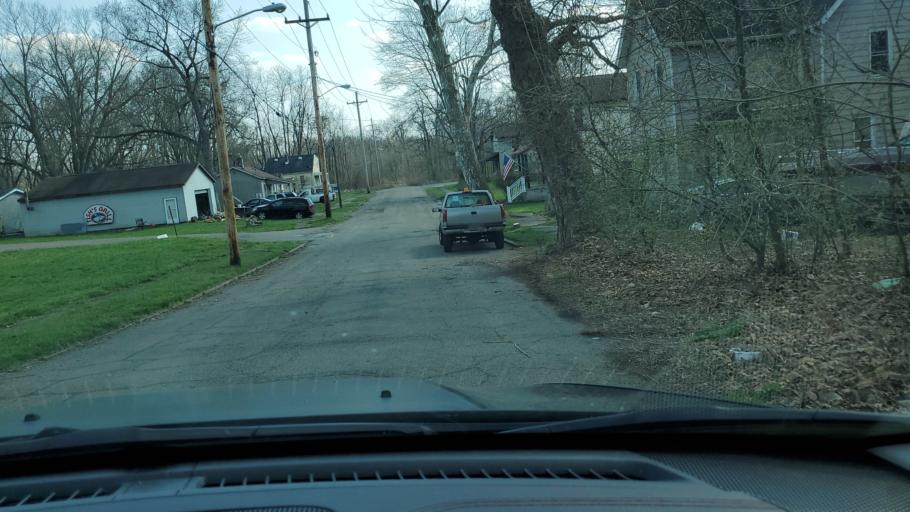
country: US
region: Ohio
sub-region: Trumbull County
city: Niles
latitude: 41.1738
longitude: -80.7528
